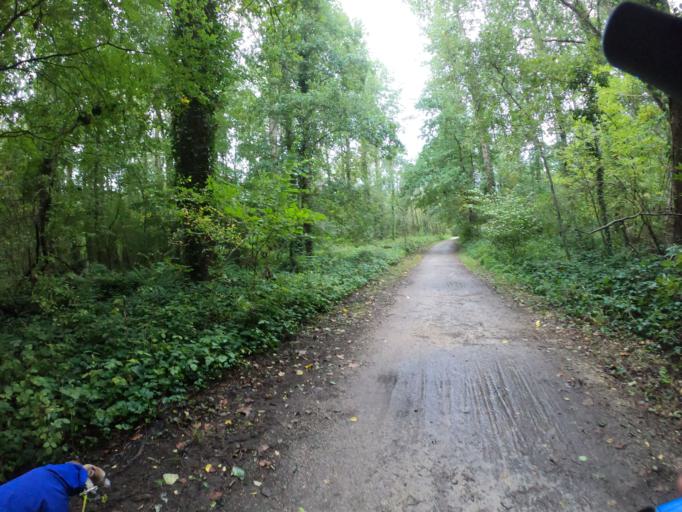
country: BE
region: Flanders
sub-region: Provincie Vlaams-Brabant
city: Rotselaar
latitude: 50.9496
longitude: 4.7331
